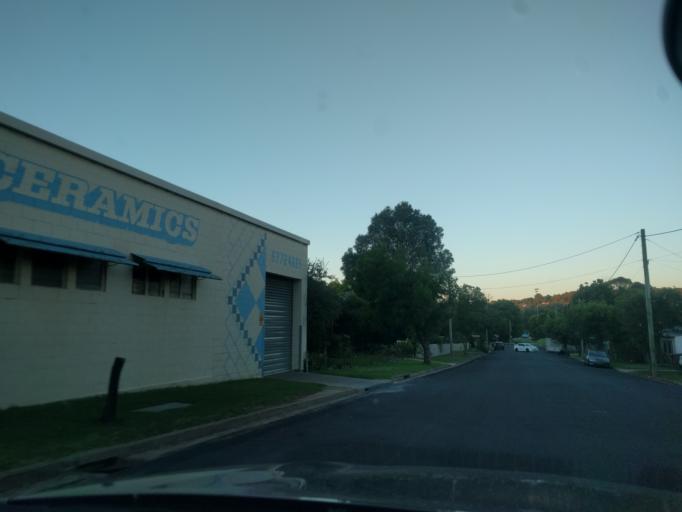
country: AU
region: New South Wales
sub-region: Armidale Dumaresq
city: Armidale
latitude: -30.5107
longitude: 151.6570
